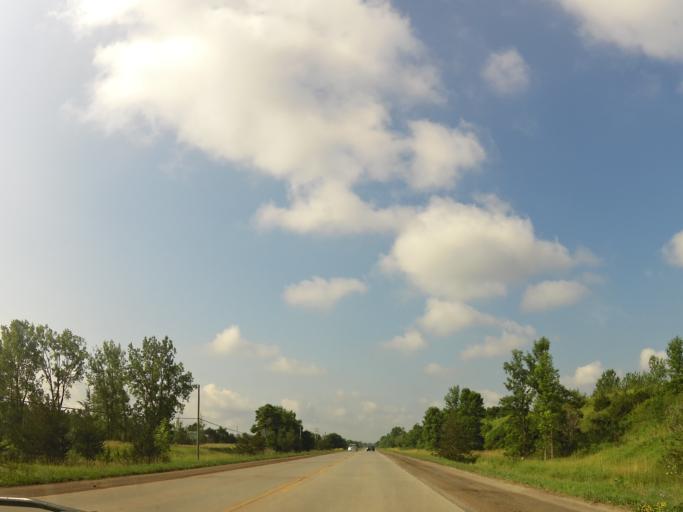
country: CA
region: Ontario
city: Picton
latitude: 44.0572
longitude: -77.1255
